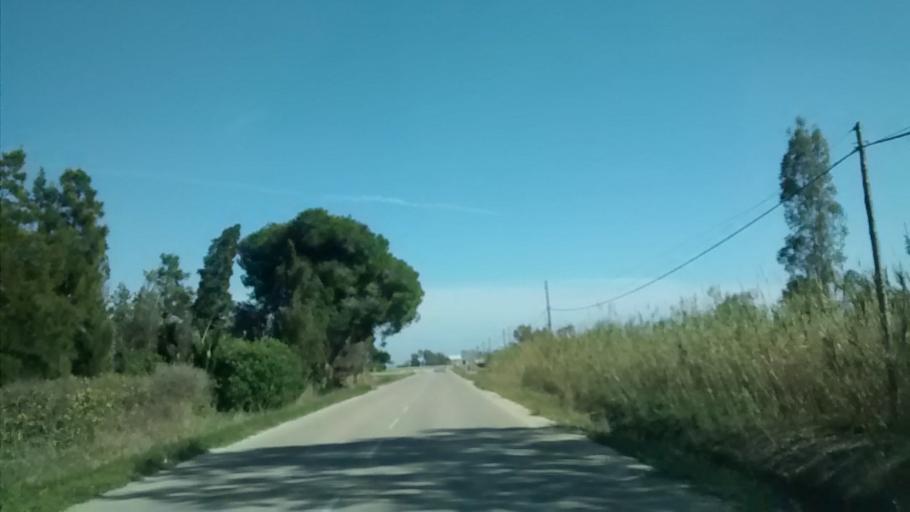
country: ES
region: Catalonia
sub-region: Provincia de Tarragona
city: Deltebre
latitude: 40.7125
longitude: 0.7538
